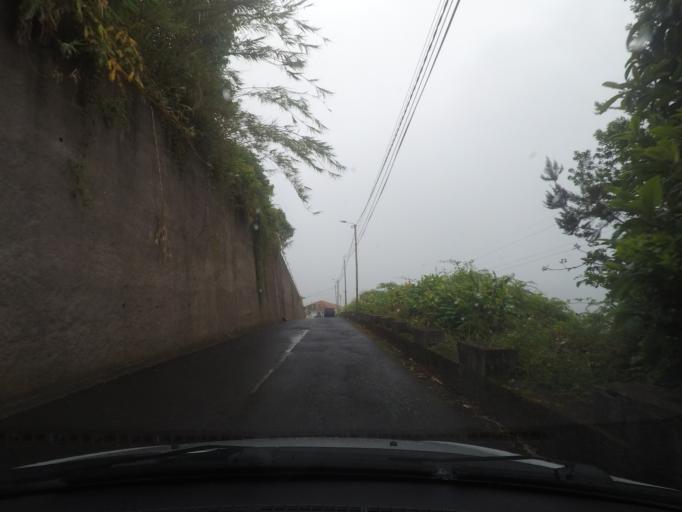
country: PT
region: Madeira
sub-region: Santana
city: Santana
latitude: 32.7774
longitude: -16.8649
